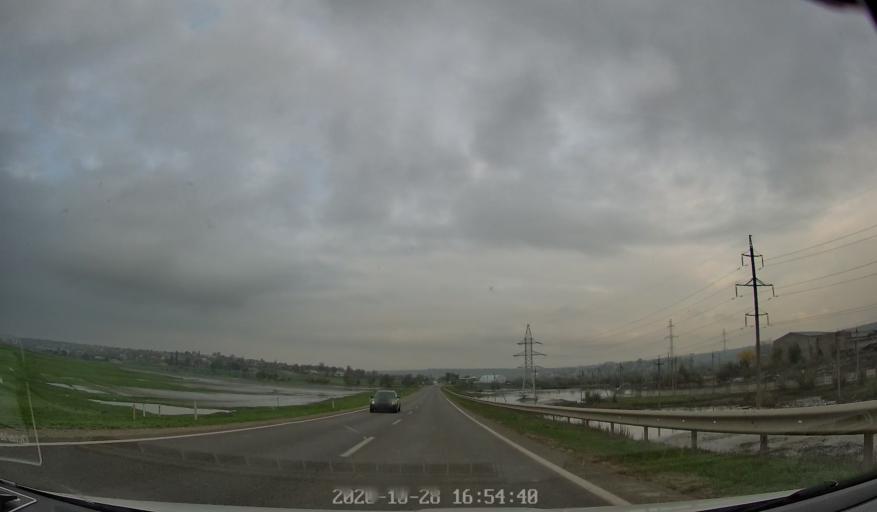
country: MD
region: Gagauzia
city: Bugeac
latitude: 46.3556
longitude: 28.6568
